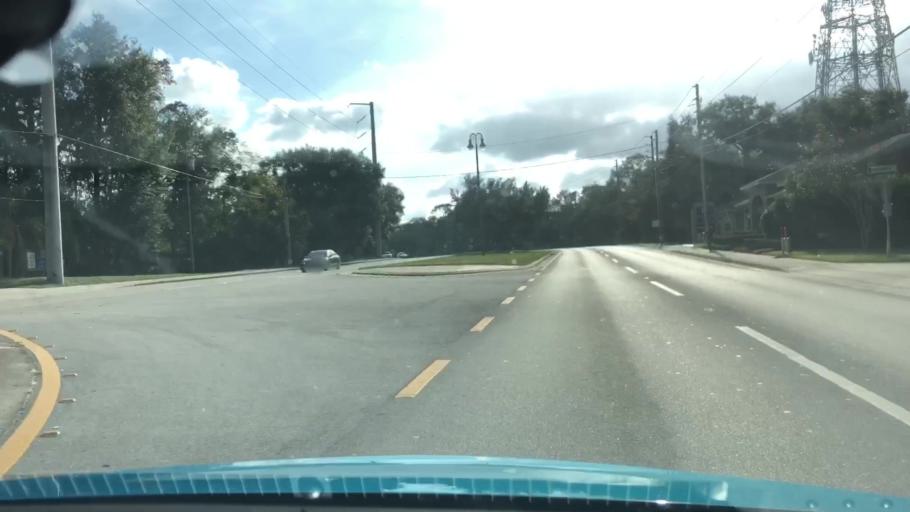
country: US
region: Florida
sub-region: Seminole County
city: Longwood
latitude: 28.7149
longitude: -81.3415
